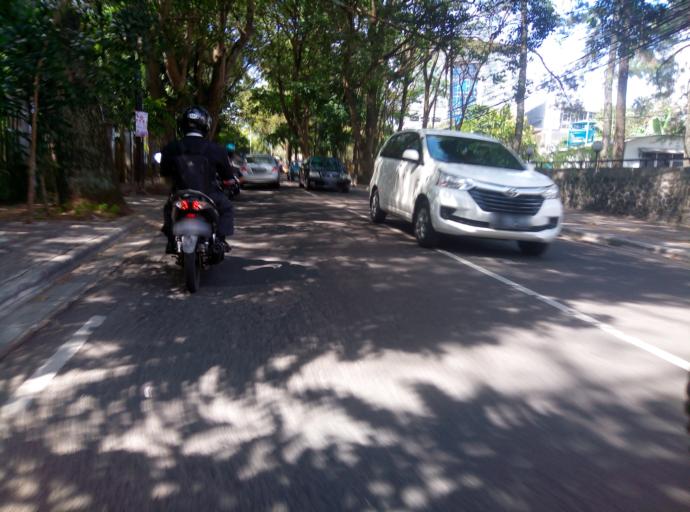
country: ID
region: West Java
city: Bandung
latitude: -6.8876
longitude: 107.6103
